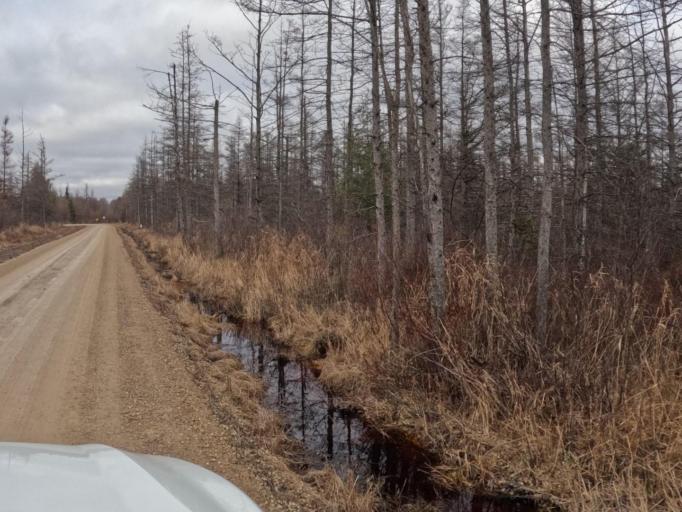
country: CA
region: Ontario
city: Shelburne
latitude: 43.9033
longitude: -80.4094
